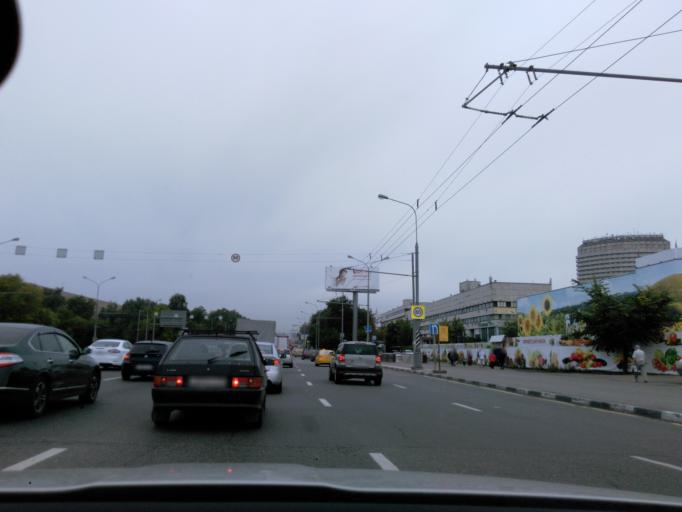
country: RU
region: Moscow
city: Tsaritsyno
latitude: 55.6554
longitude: 37.6484
